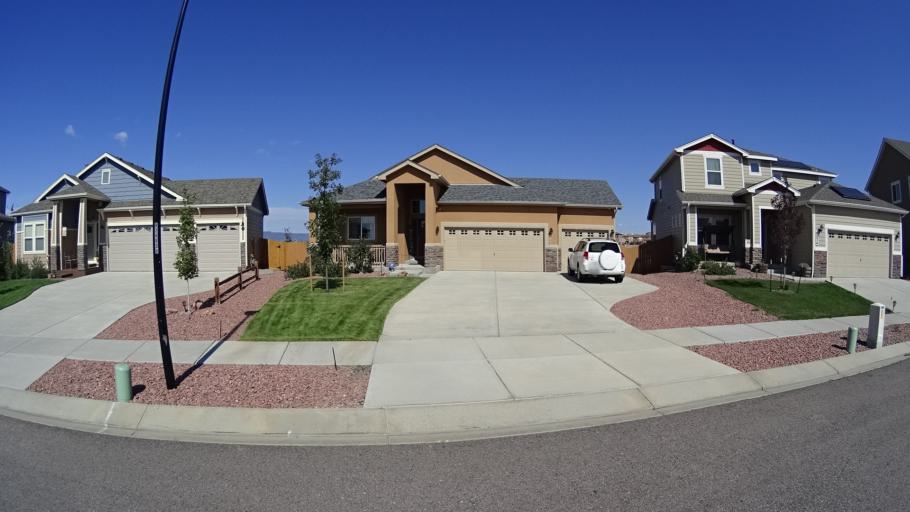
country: US
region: Colorado
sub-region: El Paso County
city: Cimarron Hills
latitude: 38.9293
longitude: -104.7120
